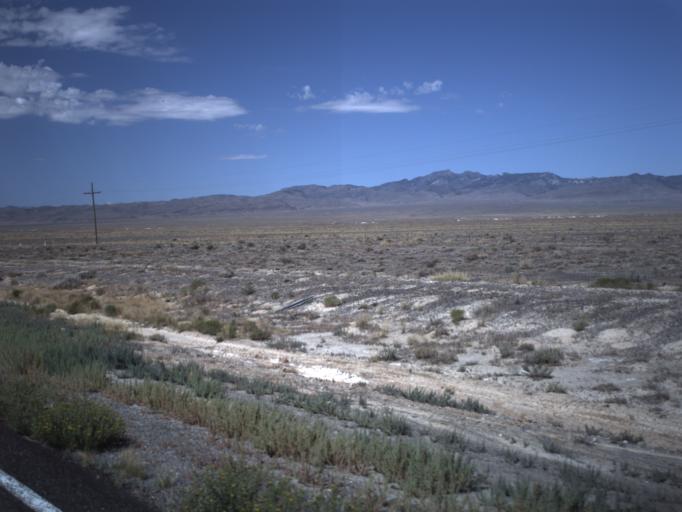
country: US
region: Utah
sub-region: Millard County
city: Delta
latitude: 39.1158
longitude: -113.1282
